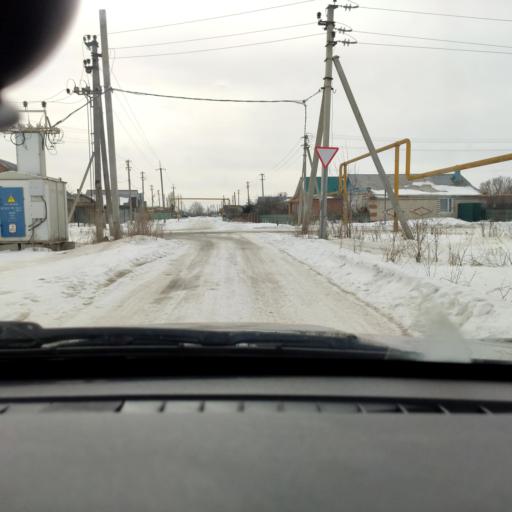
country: RU
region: Samara
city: Tol'yatti
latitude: 53.6392
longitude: 49.2880
